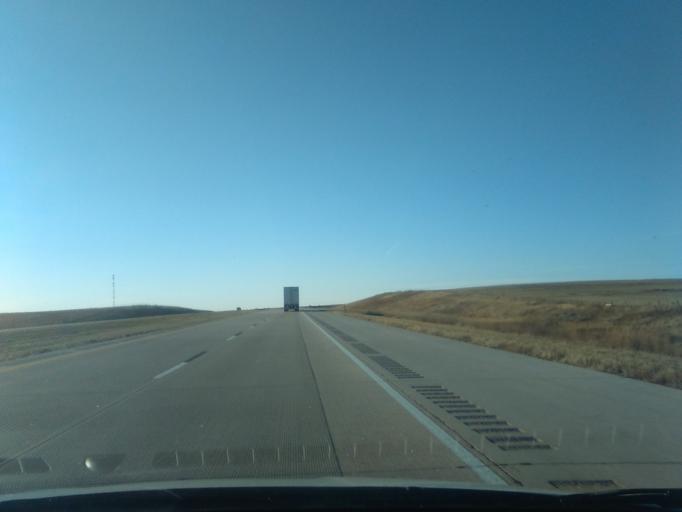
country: US
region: Nebraska
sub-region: Deuel County
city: Chappell
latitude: 41.1135
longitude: -102.6694
